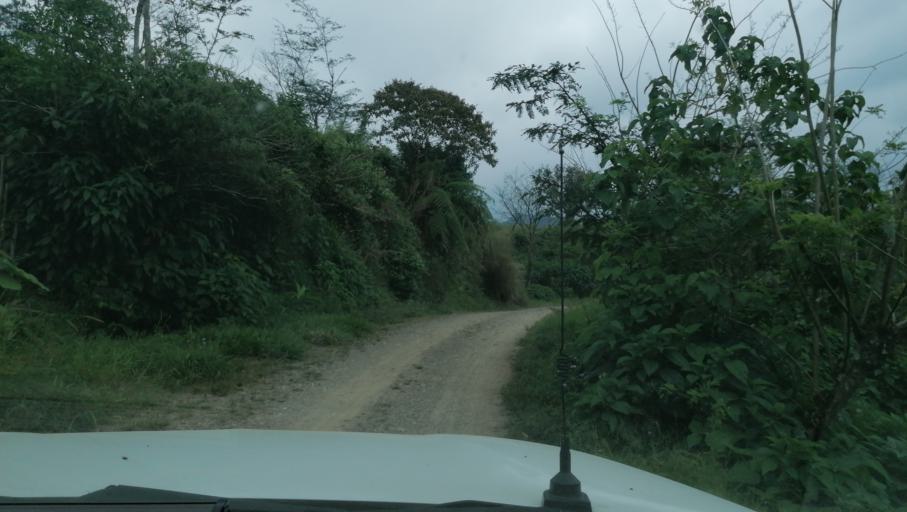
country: MX
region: Chiapas
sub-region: Francisco Leon
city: San Miguel la Sardina
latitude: 17.3377
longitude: -93.3132
